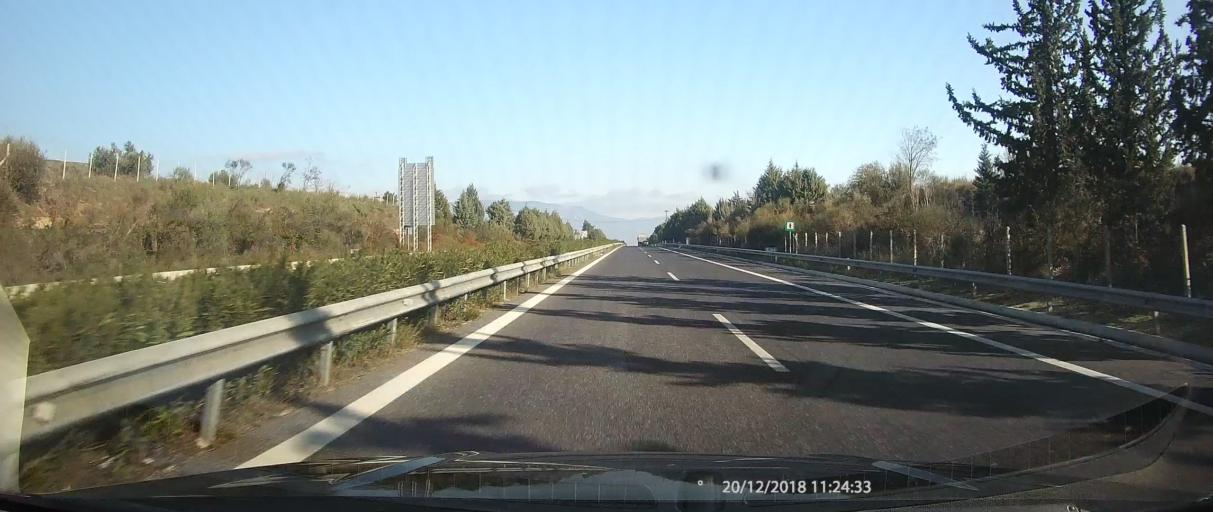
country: GR
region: Peloponnese
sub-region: Nomos Korinthias
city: Arkhaia Korinthos
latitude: 37.8801
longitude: 22.8857
